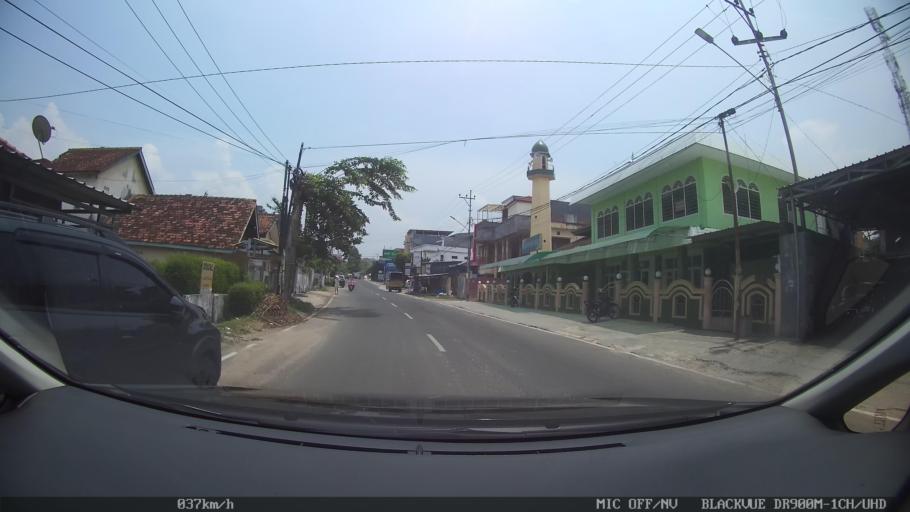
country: ID
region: Lampung
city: Bandarlampung
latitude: -5.4412
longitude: 105.2716
